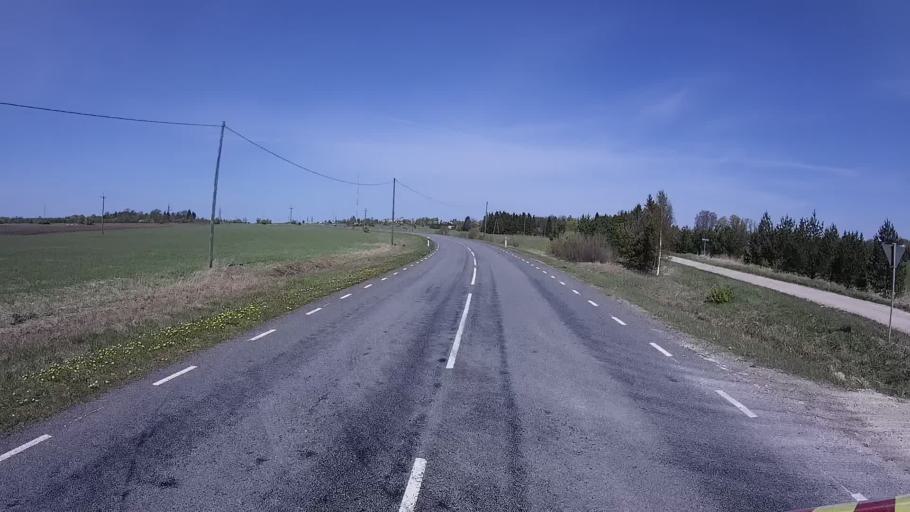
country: EE
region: Laeaene
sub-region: Lihula vald
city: Lihula
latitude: 58.6663
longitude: 23.8338
